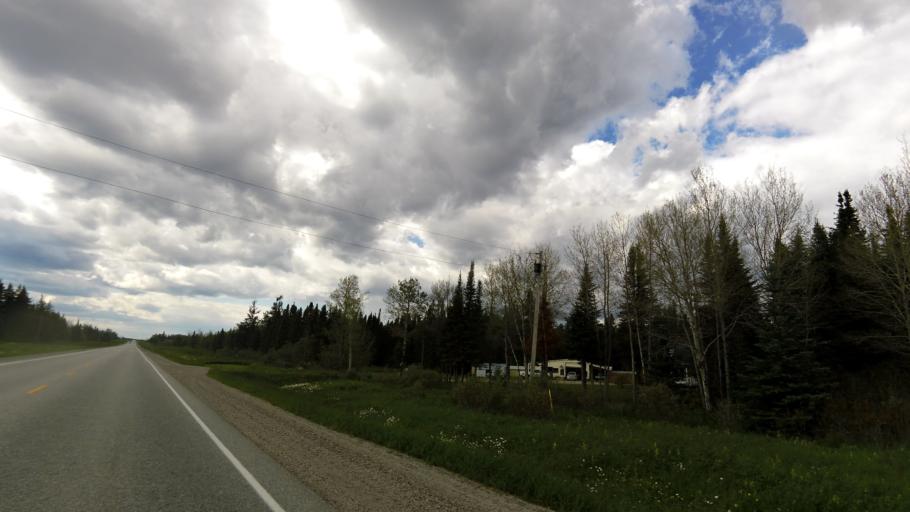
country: CA
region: Ontario
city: Hearst
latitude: 49.6980
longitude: -83.7288
